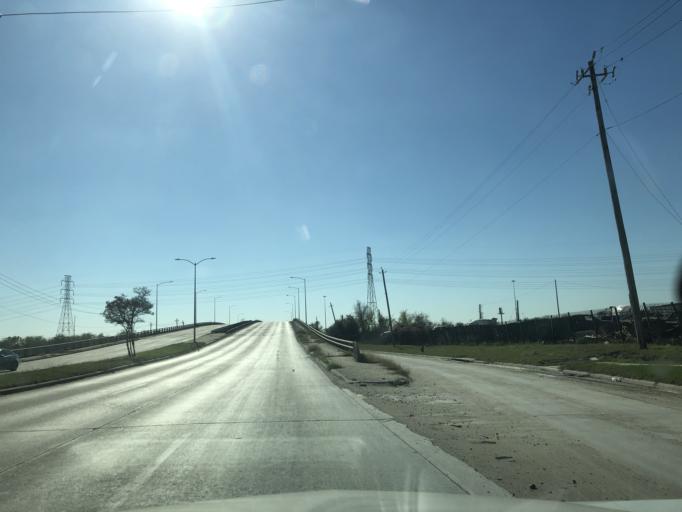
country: US
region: Texas
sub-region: Harris County
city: Houston
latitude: 29.8136
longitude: -95.3020
